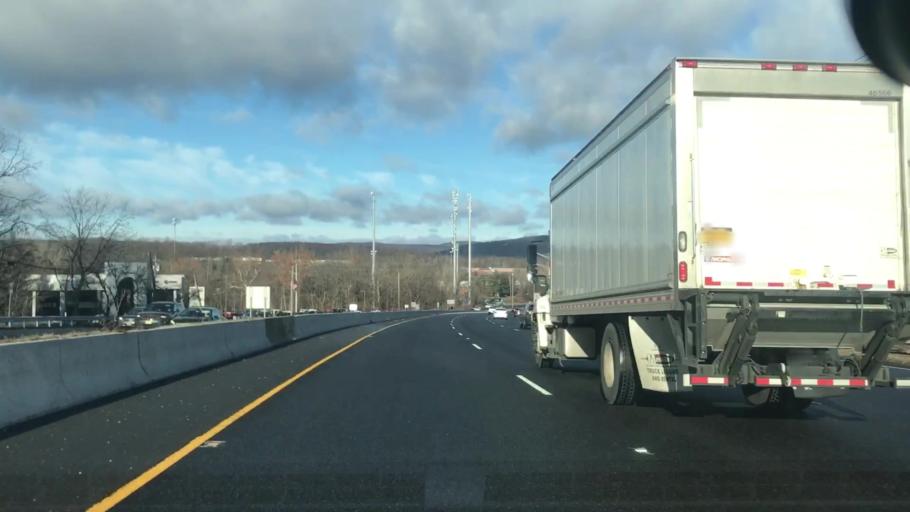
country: US
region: New Jersey
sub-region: Bergen County
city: Mahwah
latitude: 41.0763
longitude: -74.1465
